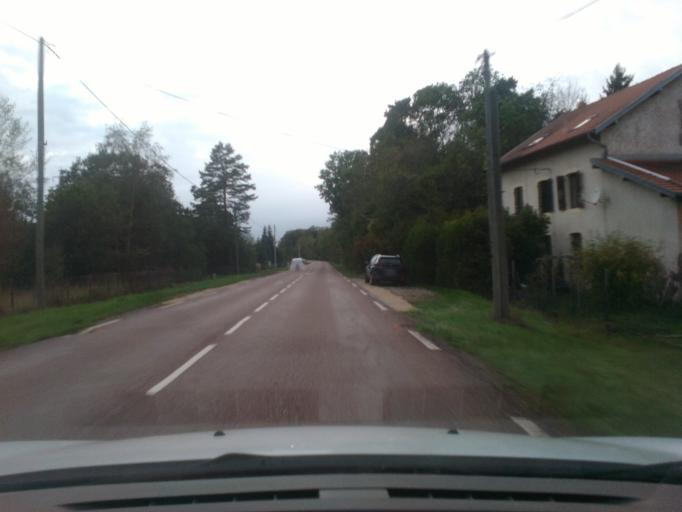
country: FR
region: Lorraine
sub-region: Departement des Vosges
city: Chatel-sur-Moselle
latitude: 48.3489
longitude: 6.3998
